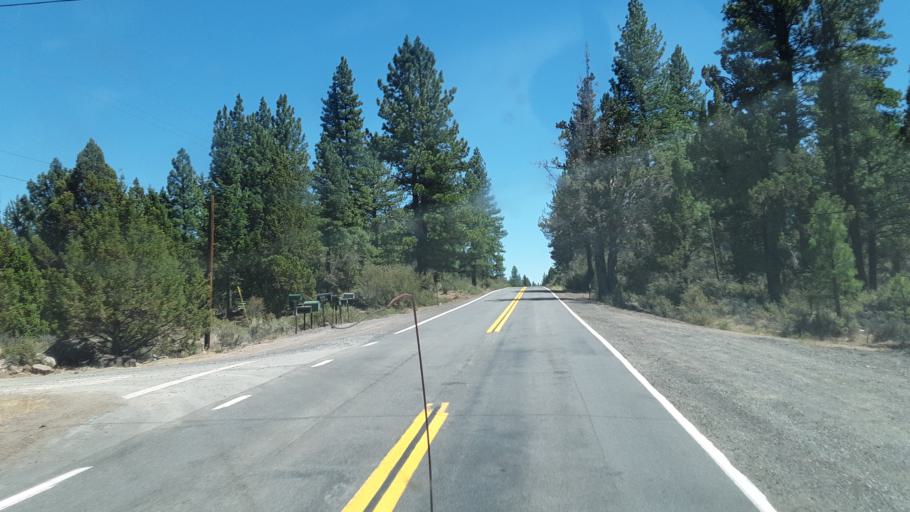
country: US
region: California
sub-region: Lassen County
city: Susanville
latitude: 40.5137
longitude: -120.5764
